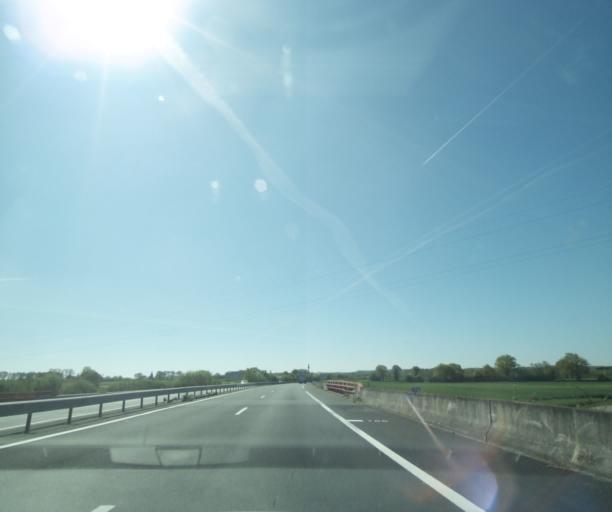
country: FR
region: Centre
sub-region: Departement de l'Indre
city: Le Pechereau
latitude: 46.5210
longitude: 1.5141
